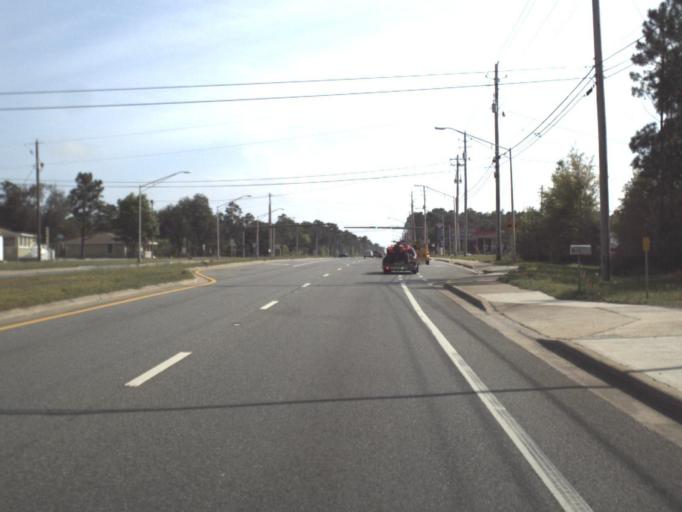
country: US
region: Florida
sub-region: Santa Rosa County
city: Navarre
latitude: 30.4341
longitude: -86.8658
